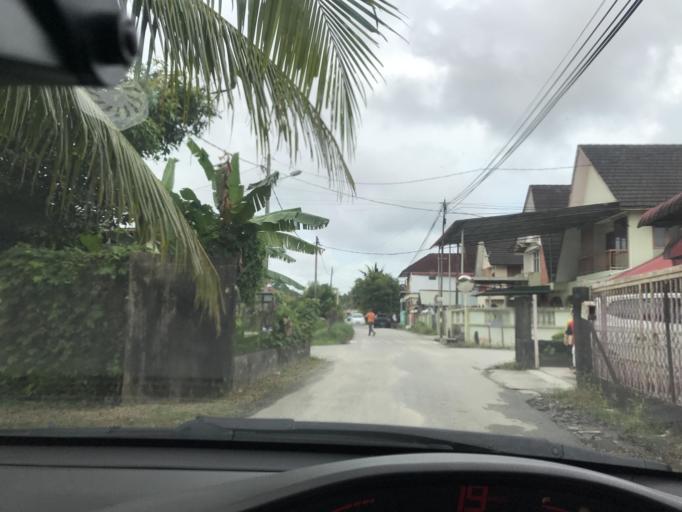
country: MY
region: Kelantan
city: Kota Bharu
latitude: 6.1139
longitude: 102.2170
